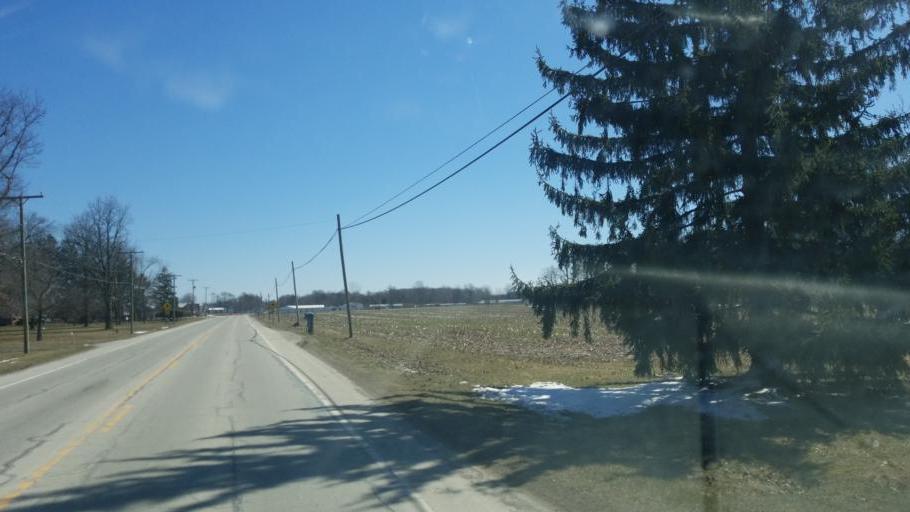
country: US
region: Ohio
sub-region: Crawford County
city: Galion
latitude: 40.8132
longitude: -82.8602
